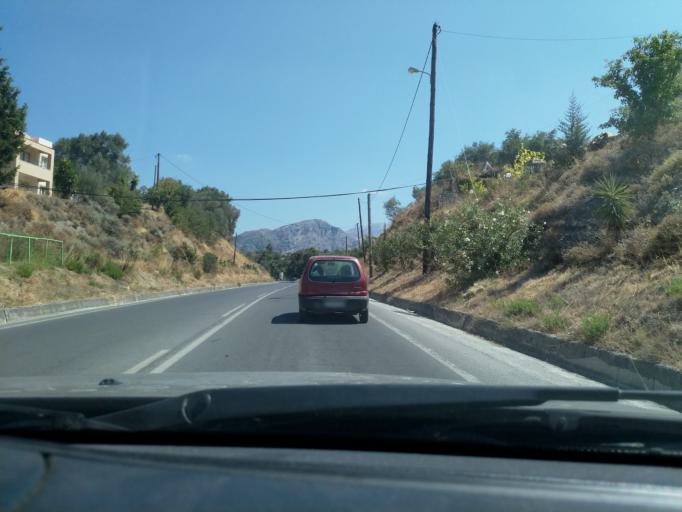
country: GR
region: Crete
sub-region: Nomos Rethymnis
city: Agia Foteini
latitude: 35.2216
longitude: 24.4958
